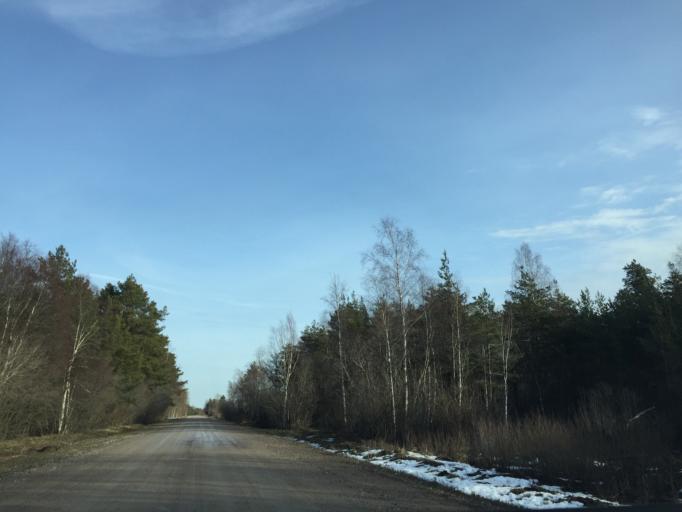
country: EE
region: Saare
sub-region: Kuressaare linn
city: Kuressaare
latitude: 58.3185
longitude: 21.9942
